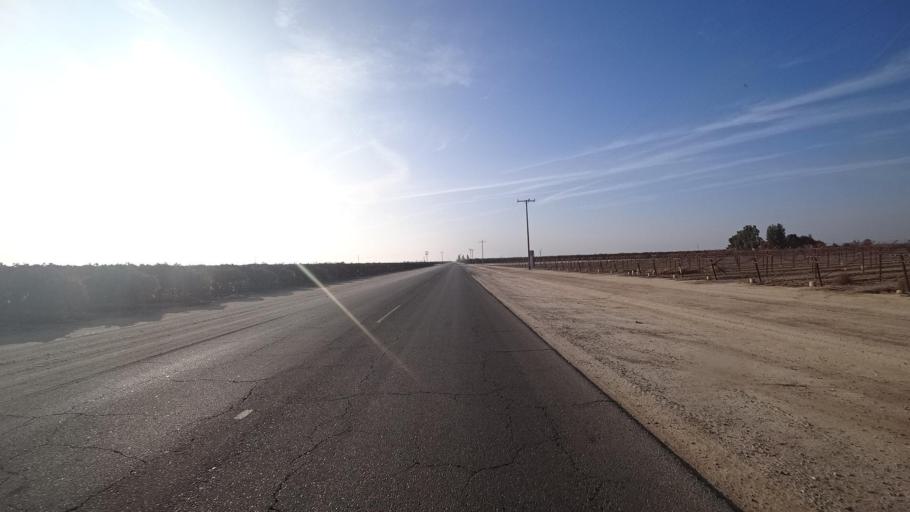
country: US
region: California
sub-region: Kern County
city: Delano
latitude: 35.7712
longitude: -119.1876
